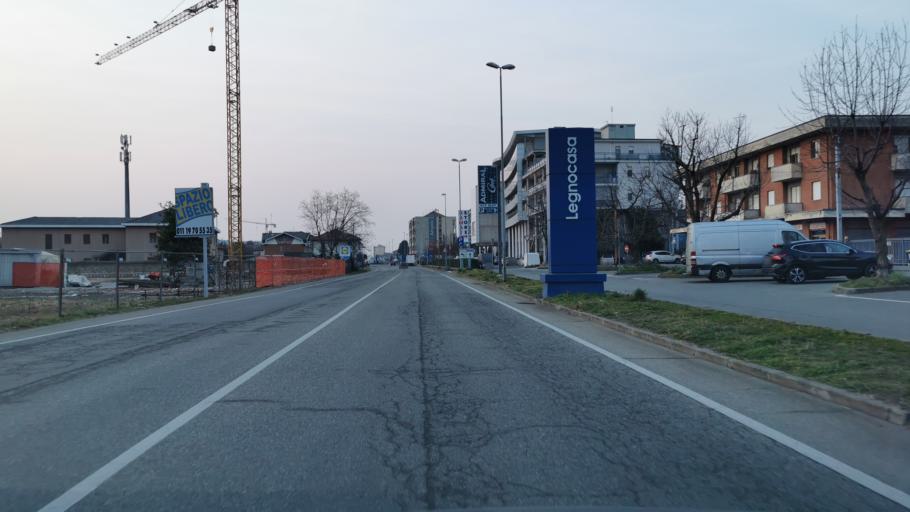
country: IT
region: Piedmont
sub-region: Provincia di Torino
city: Borgaro Torinese
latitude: 45.1543
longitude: 7.6547
